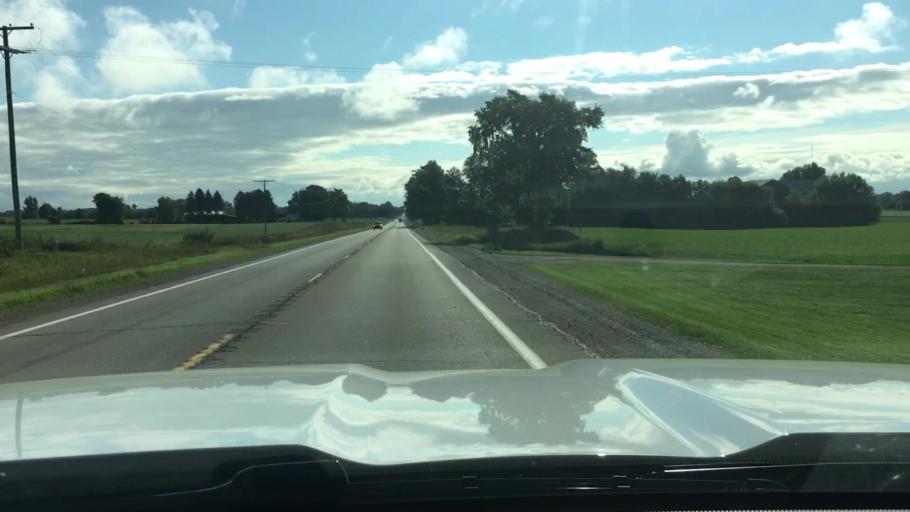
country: US
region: Michigan
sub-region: Tuscola County
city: Cass City
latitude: 43.6003
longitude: -83.2048
